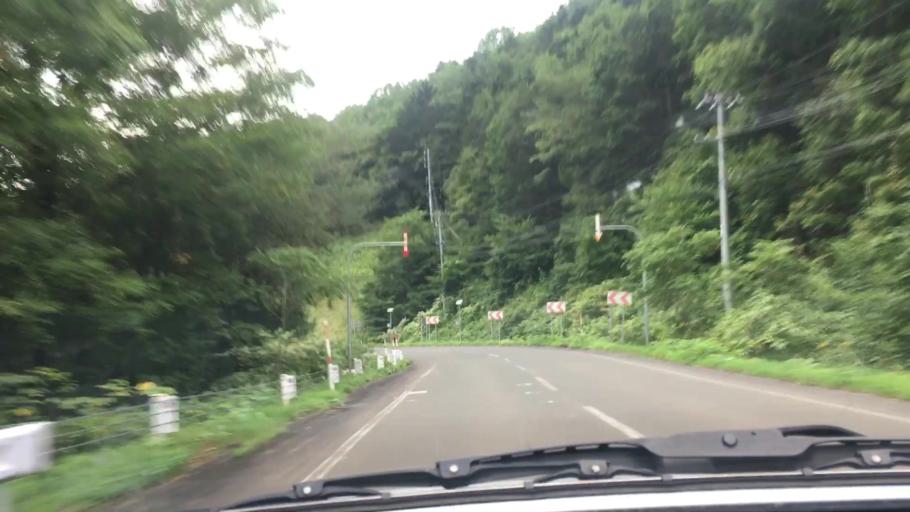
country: JP
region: Hokkaido
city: Shimo-furano
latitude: 43.0485
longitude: 142.5132
